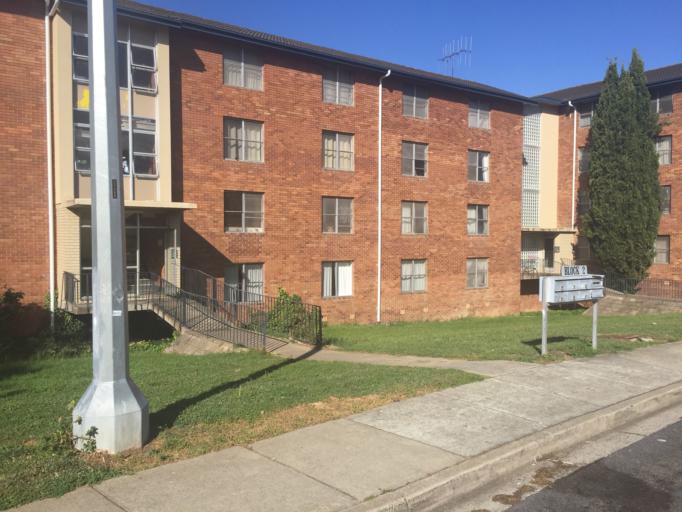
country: AU
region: Australian Capital Territory
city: Forrest
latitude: -35.3212
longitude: 149.1370
